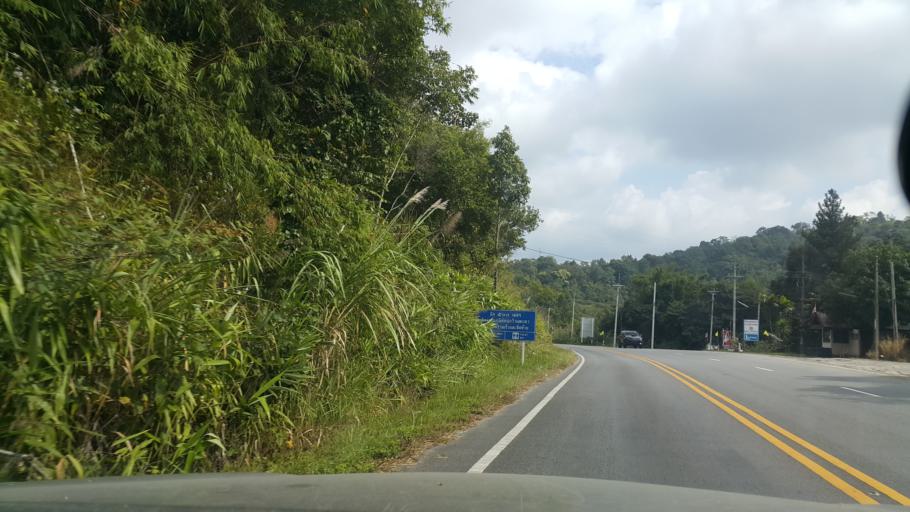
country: TH
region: Phayao
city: Phayao
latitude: 19.0612
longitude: 99.7773
